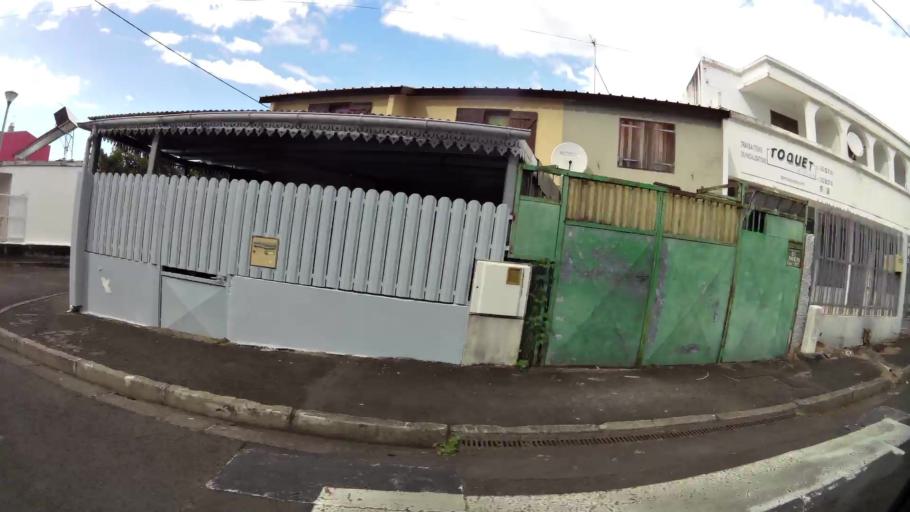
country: RE
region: Reunion
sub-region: Reunion
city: Saint-Denis
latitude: -20.8921
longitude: 55.4773
